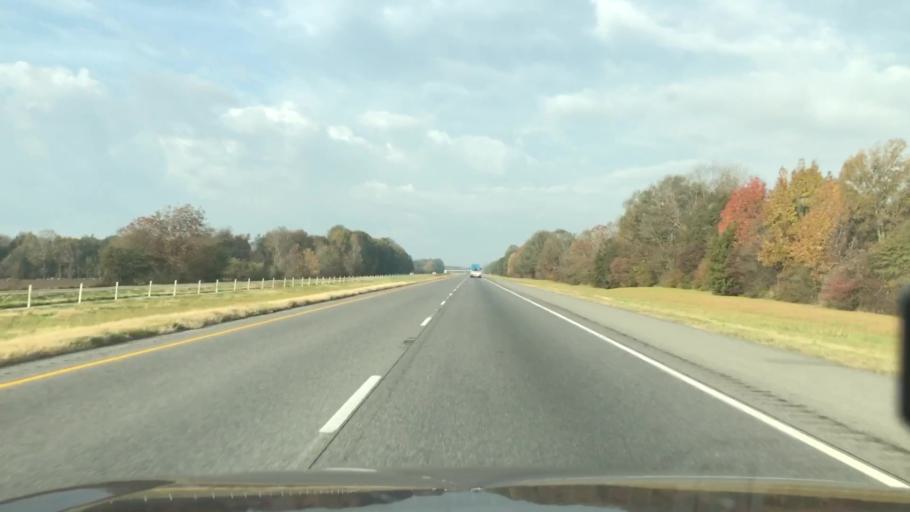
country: US
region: Louisiana
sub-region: Richland Parish
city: Delhi
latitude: 32.4234
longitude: -91.3518
